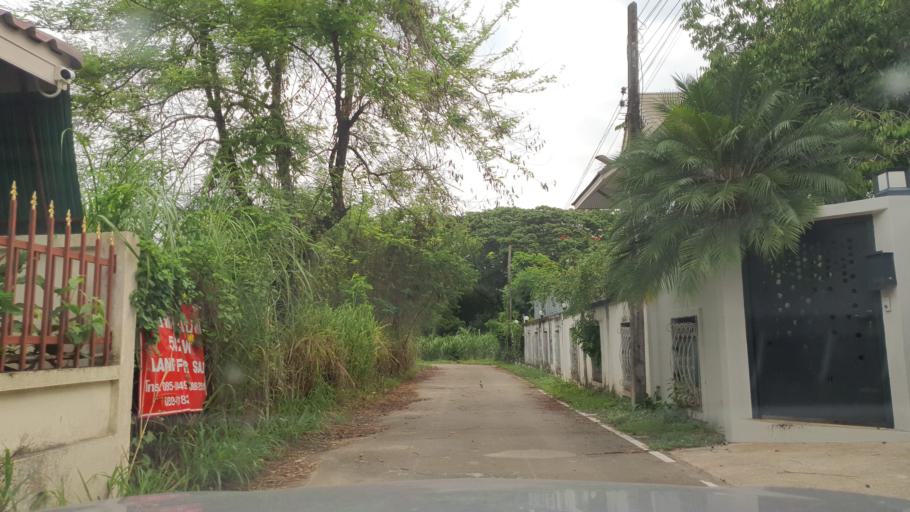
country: TH
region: Chiang Mai
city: Hang Dong
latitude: 18.7489
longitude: 98.9316
